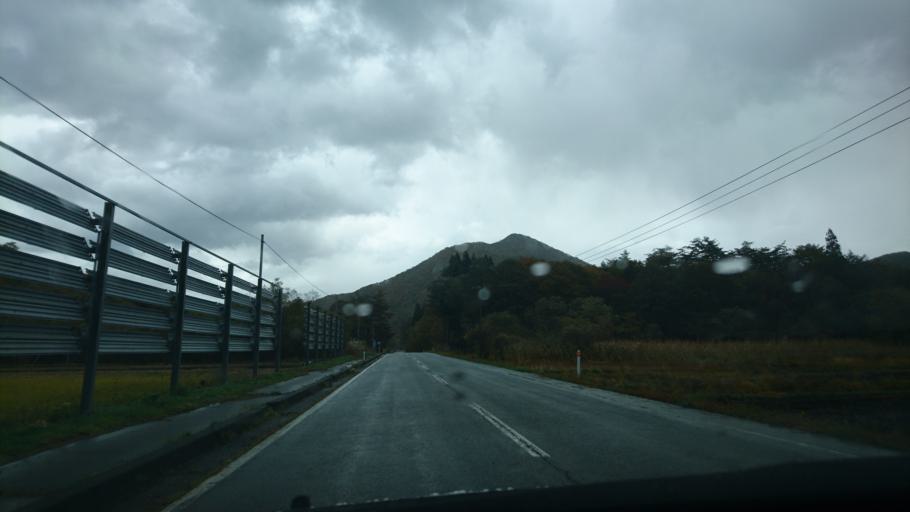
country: JP
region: Iwate
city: Shizukuishi
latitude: 39.6088
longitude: 140.9365
